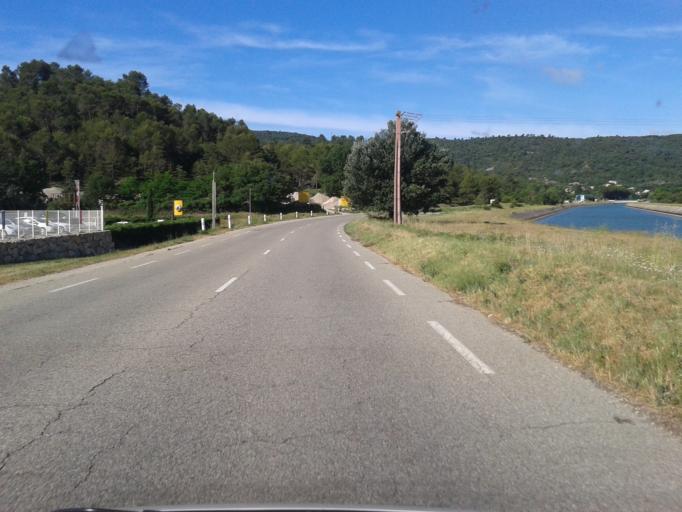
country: FR
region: Provence-Alpes-Cote d'Azur
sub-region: Departement du Vaucluse
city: Beaumont-de-Pertuis
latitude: 43.6894
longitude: 5.7217
